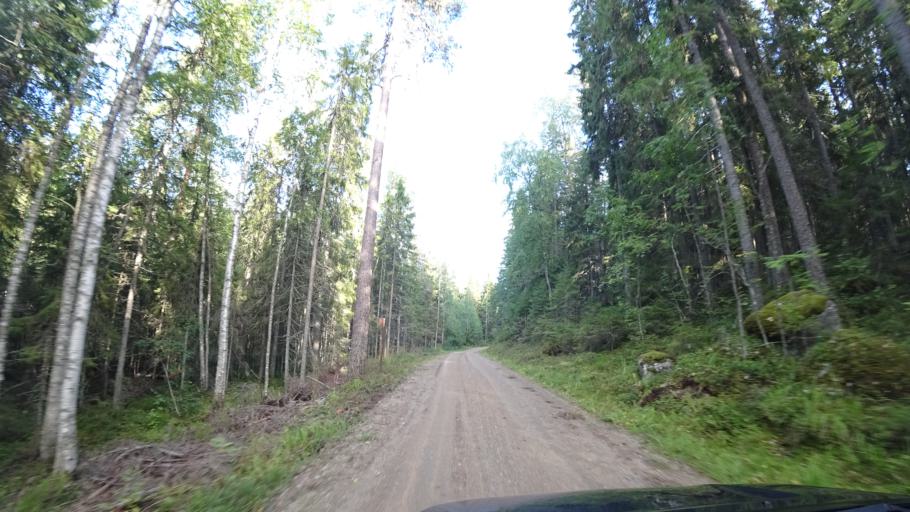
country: FI
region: Paijanne Tavastia
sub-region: Lahti
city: Auttoinen
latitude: 61.2216
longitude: 25.2000
